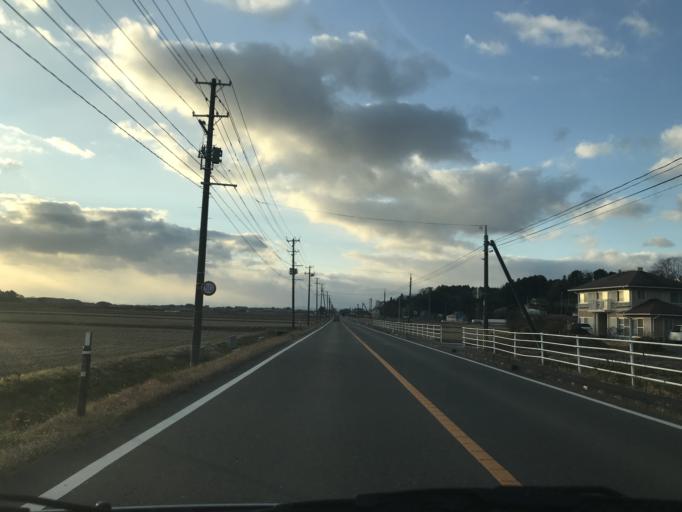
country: JP
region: Miyagi
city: Kogota
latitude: 38.6551
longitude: 141.0428
